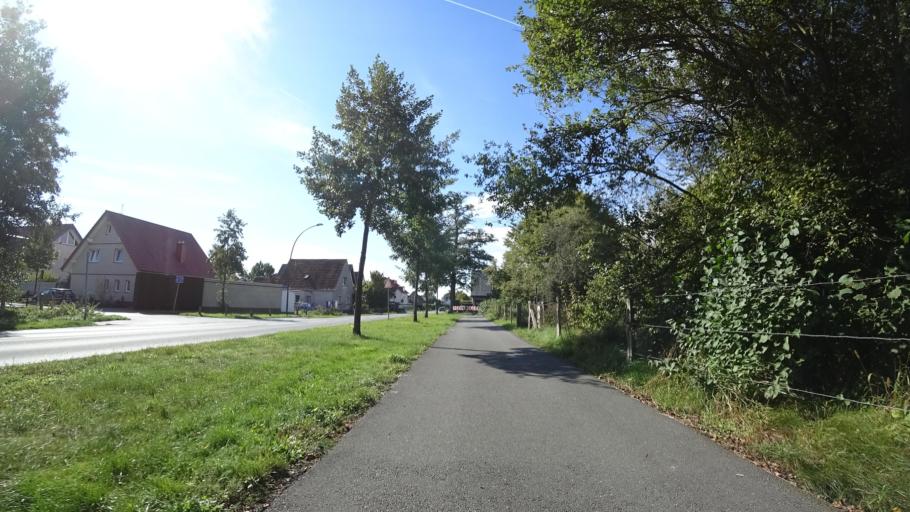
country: DE
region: North Rhine-Westphalia
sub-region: Regierungsbezirk Detmold
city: Guetersloh
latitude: 51.9293
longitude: 8.4414
